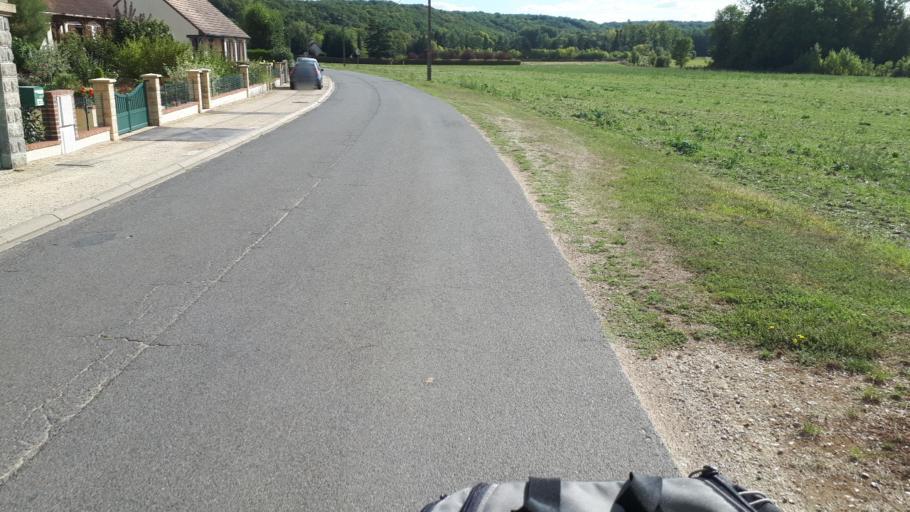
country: FR
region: Centre
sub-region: Departement du Loir-et-Cher
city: Villiers-sur-Loir
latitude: 47.7829
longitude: 0.9624
